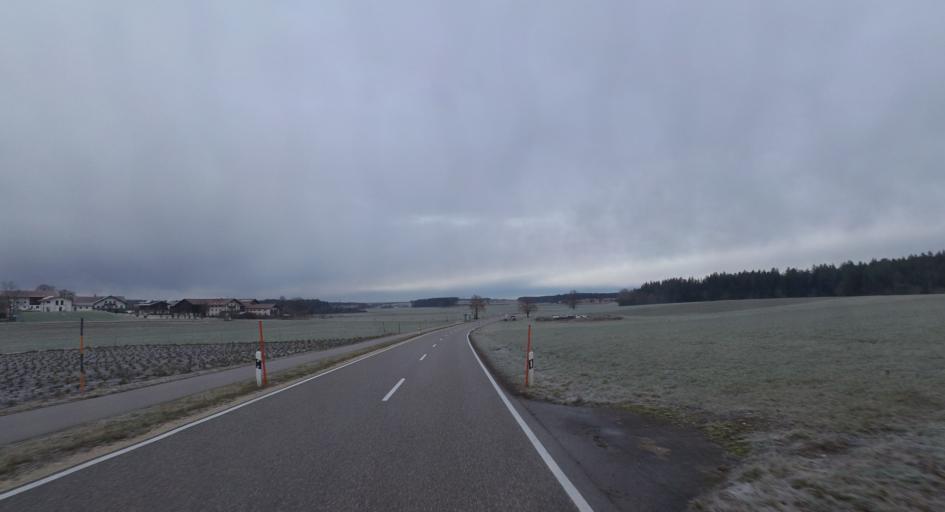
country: DE
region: Bavaria
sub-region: Upper Bavaria
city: Nussdorf
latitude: 47.9289
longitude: 12.6498
